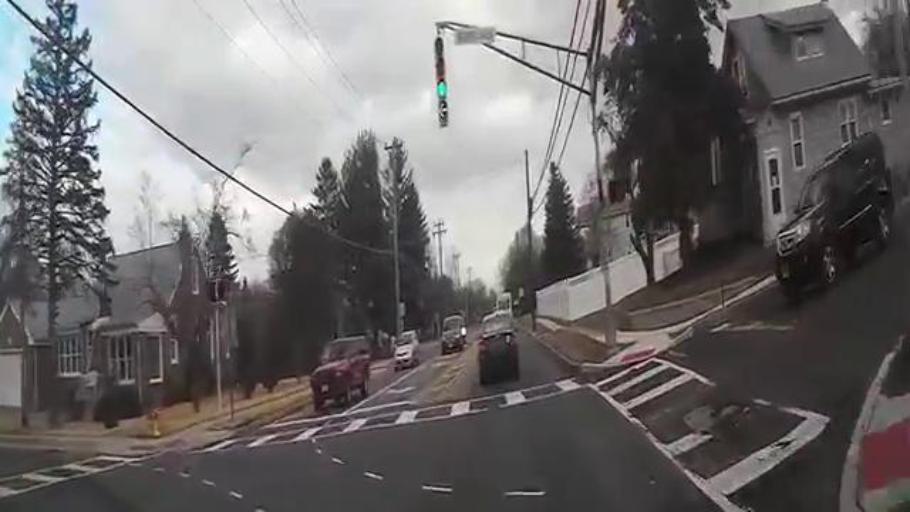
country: US
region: New Jersey
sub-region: Camden County
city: Berlin
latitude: 39.8001
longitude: -74.9497
